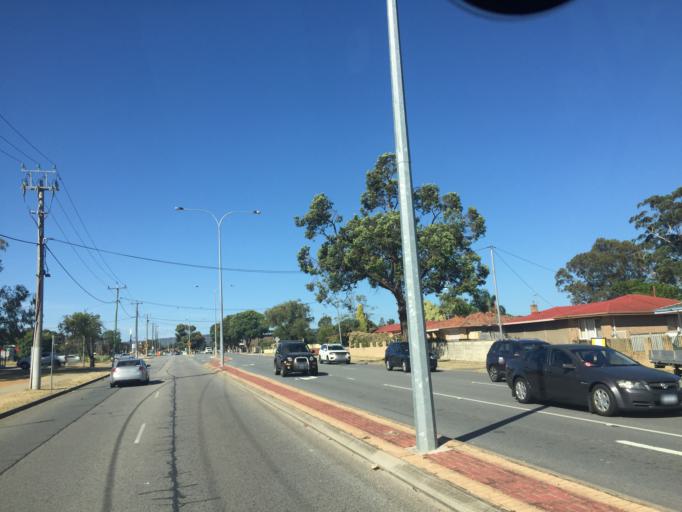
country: AU
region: Western Australia
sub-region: Gosnells
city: Maddington
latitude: -32.0533
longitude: 115.9820
